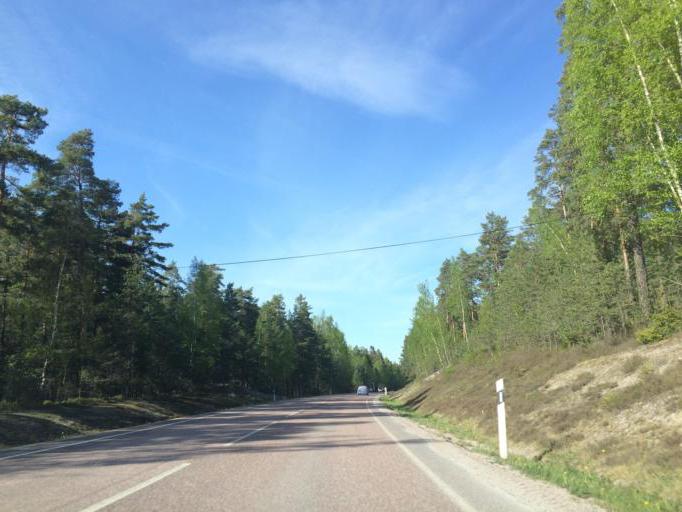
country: SE
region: Vaestmanland
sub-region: Kungsors Kommun
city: Kungsoer
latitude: 59.3794
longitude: 16.1073
